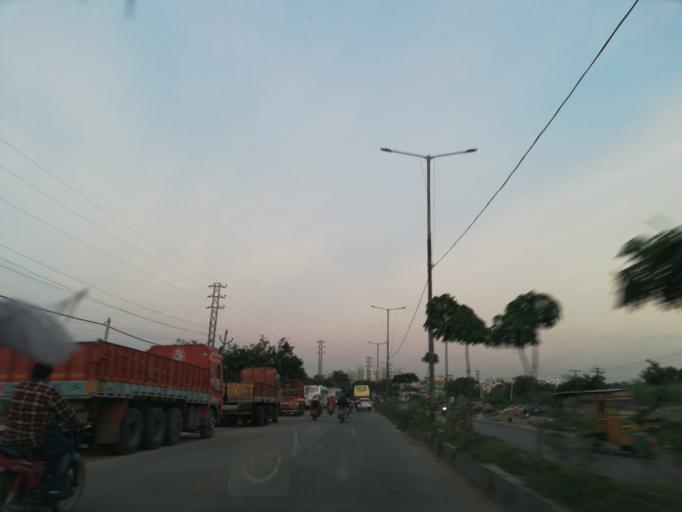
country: IN
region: Telangana
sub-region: Medak
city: Serilingampalle
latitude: 17.5159
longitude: 78.3588
